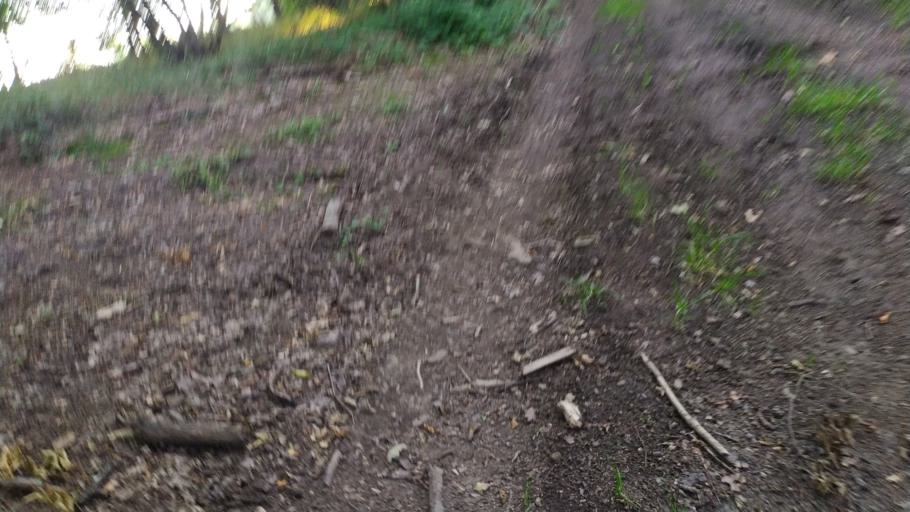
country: BE
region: Wallonia
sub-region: Province de Namur
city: Houyet
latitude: 50.2038
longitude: 5.0328
